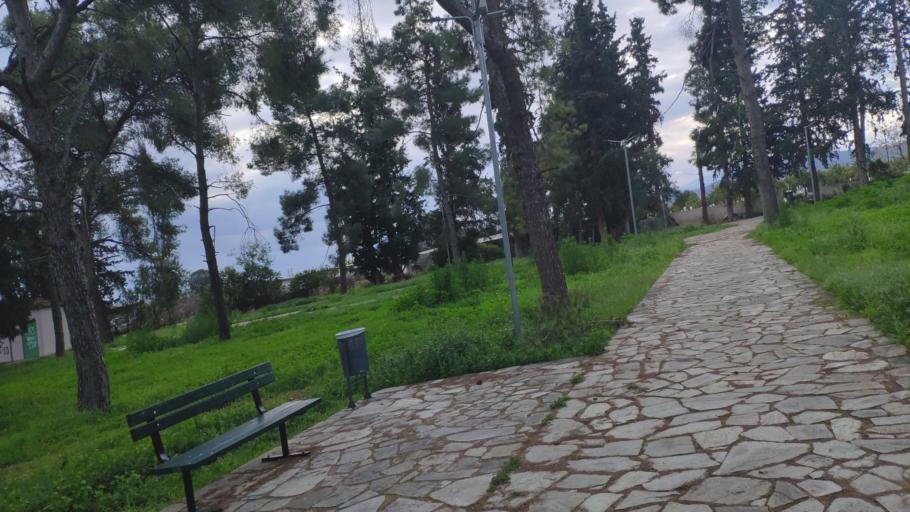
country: GR
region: Peloponnese
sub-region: Nomos Argolidos
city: Nea Kios
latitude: 37.5950
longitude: 22.6884
